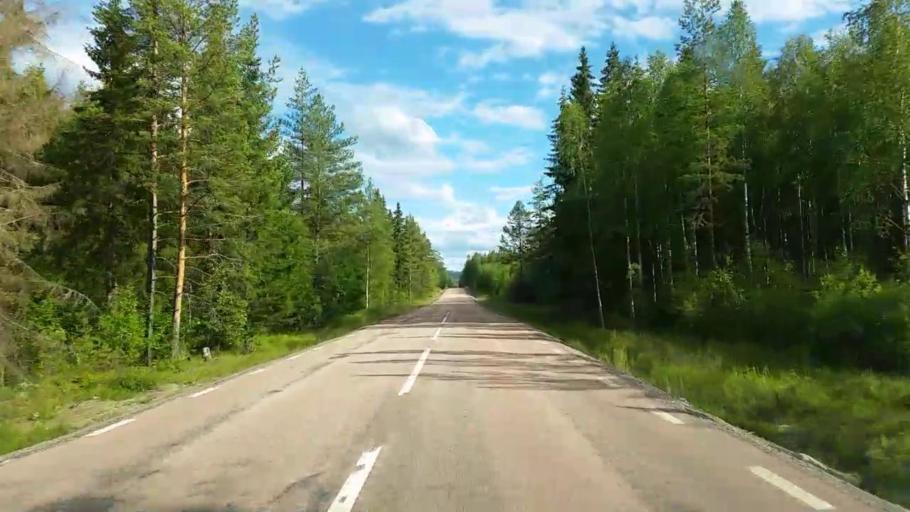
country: SE
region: Gaevleborg
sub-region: Ljusdals Kommun
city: Farila
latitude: 61.9210
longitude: 15.8764
